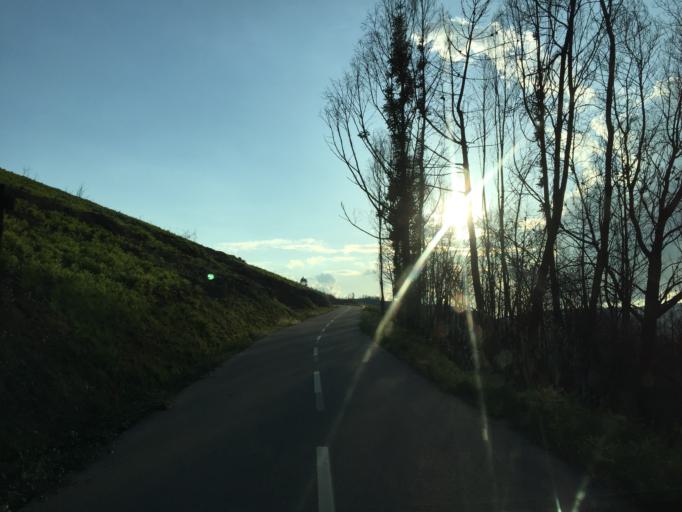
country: PT
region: Coimbra
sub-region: Pampilhosa da Serra
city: Pampilhosa da Serra
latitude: 40.1337
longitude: -7.9954
